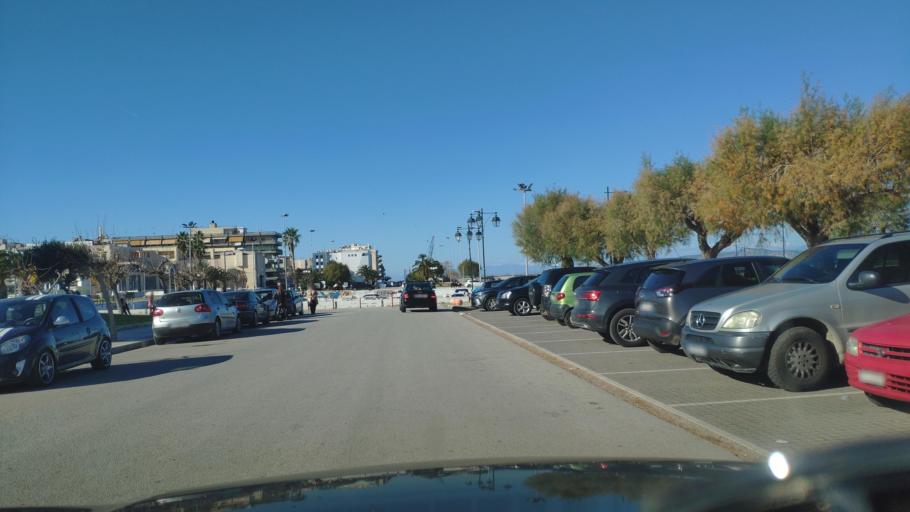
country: GR
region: Peloponnese
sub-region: Nomos Korinthias
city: Korinthos
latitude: 37.9404
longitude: 22.9360
